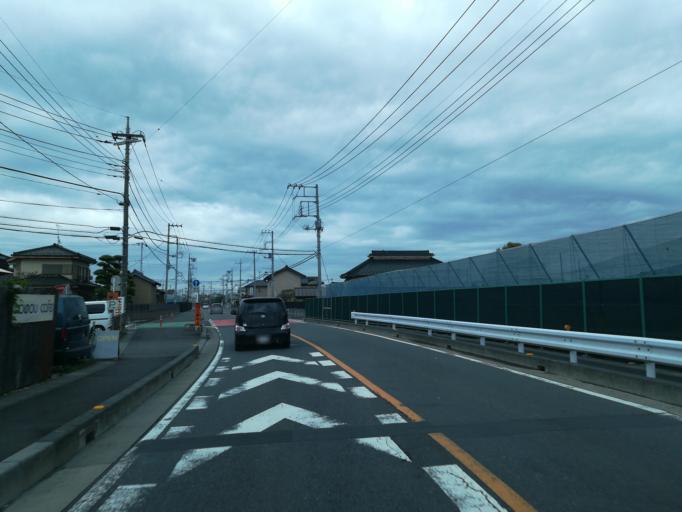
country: JP
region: Saitama
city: Shiraoka
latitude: 35.9937
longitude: 139.6651
